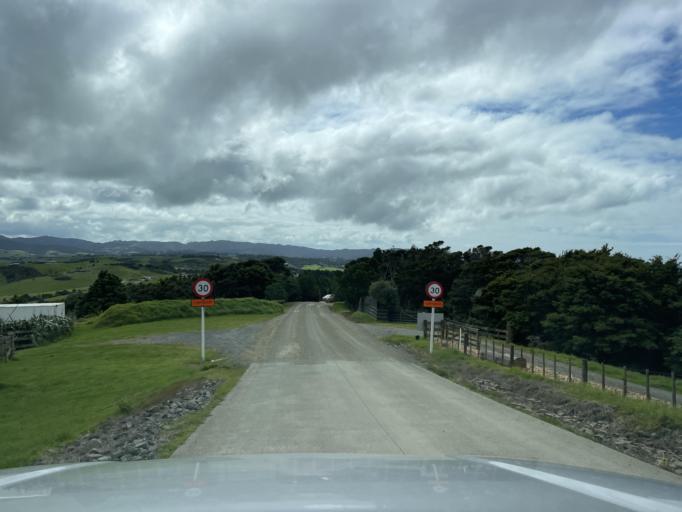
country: NZ
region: Auckland
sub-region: Auckland
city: Wellsford
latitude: -36.1653
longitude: 174.5523
